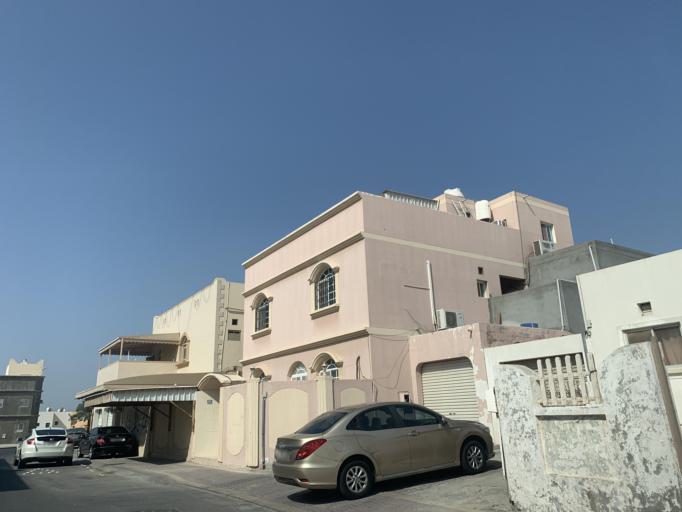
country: BH
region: Central Governorate
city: Madinat Hamad
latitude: 26.1300
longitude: 50.5028
